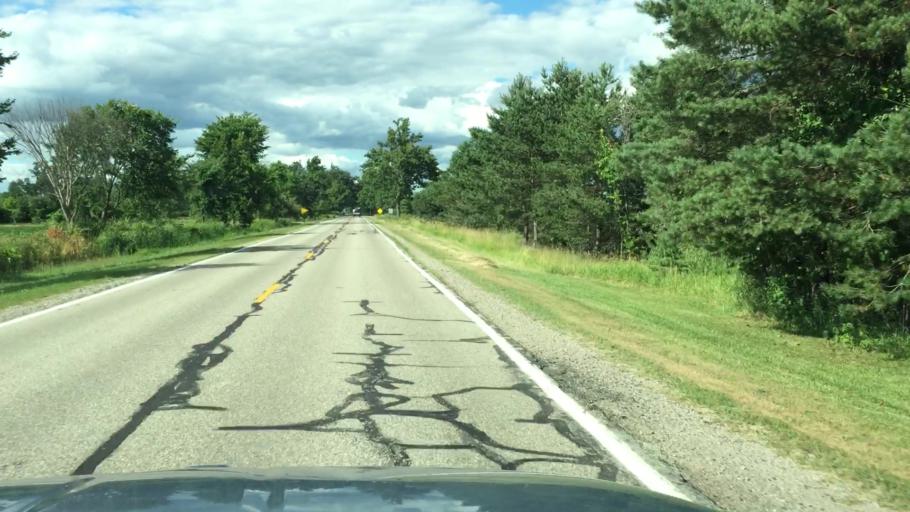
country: US
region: Michigan
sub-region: Saint Clair County
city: Capac
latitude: 43.0879
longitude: -82.9115
